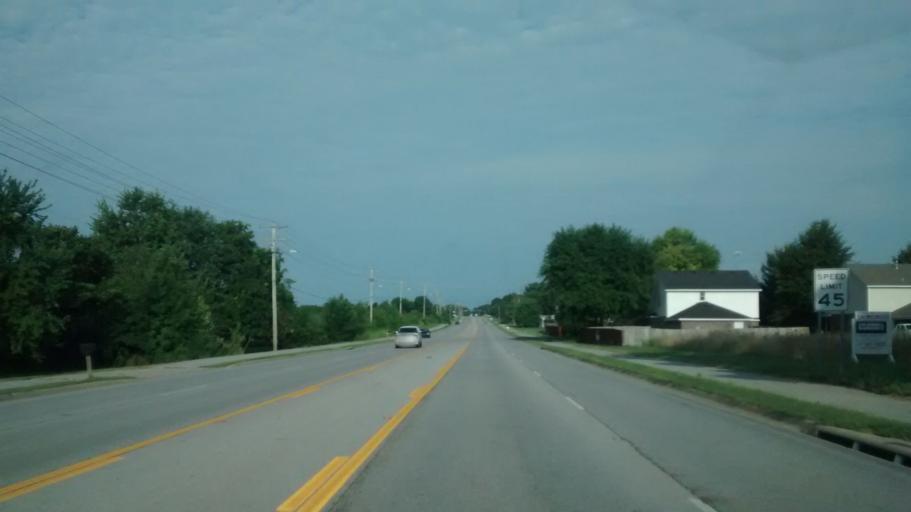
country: US
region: Arkansas
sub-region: Washington County
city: Farmington
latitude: 36.0792
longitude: -94.2423
